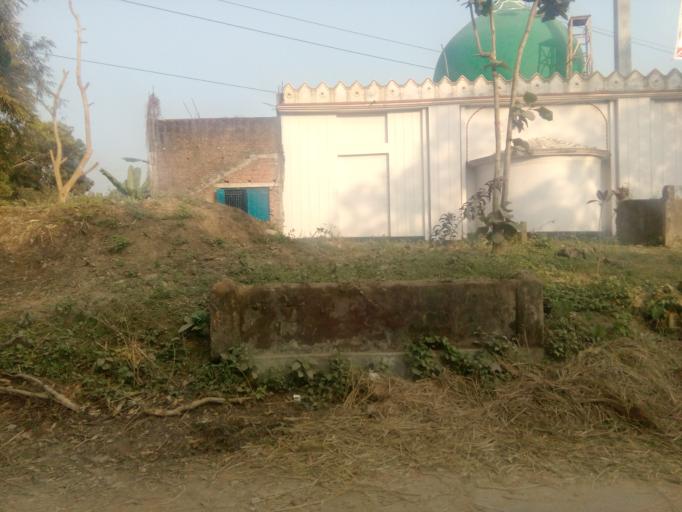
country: IN
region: Tripura
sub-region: West Tripura
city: Sonamura
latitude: 23.3218
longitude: 91.2757
